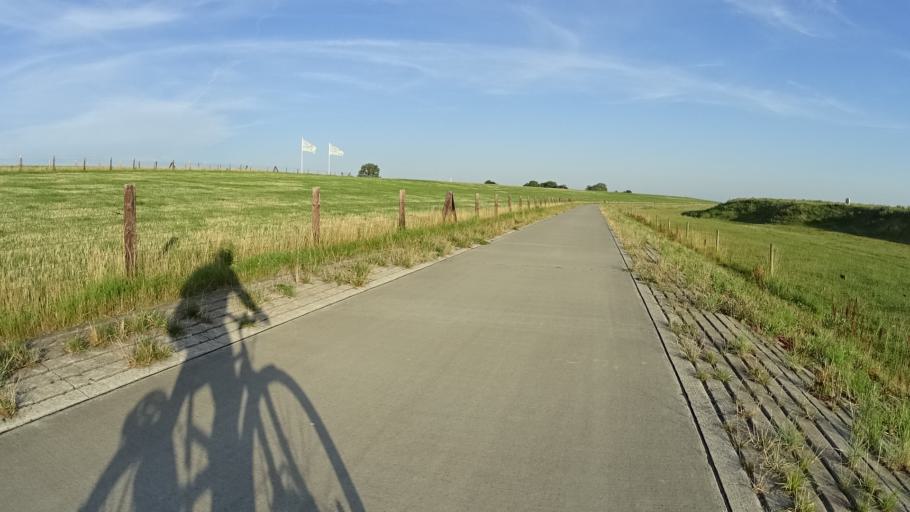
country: DE
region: Lower Saxony
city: Butjadingen
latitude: 53.6075
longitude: 8.3263
